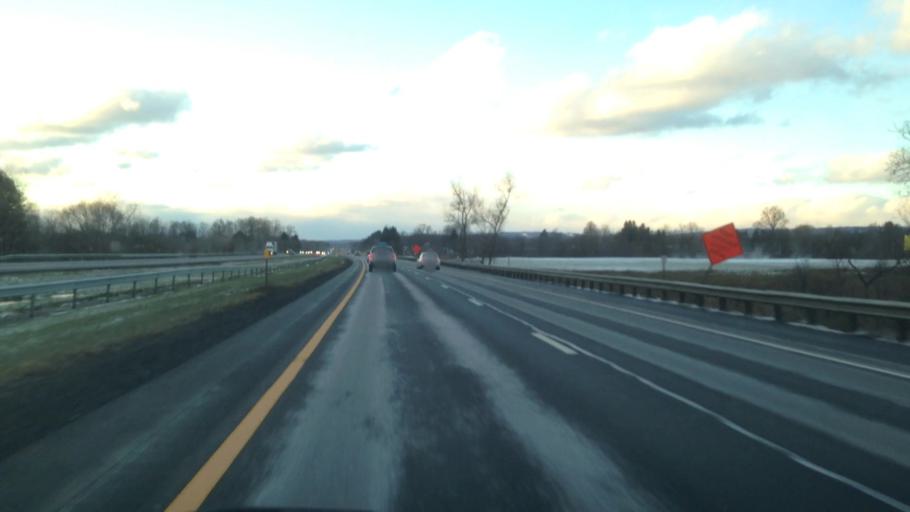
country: US
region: New York
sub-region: Herkimer County
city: Frankfort
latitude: 43.0588
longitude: -75.0722
